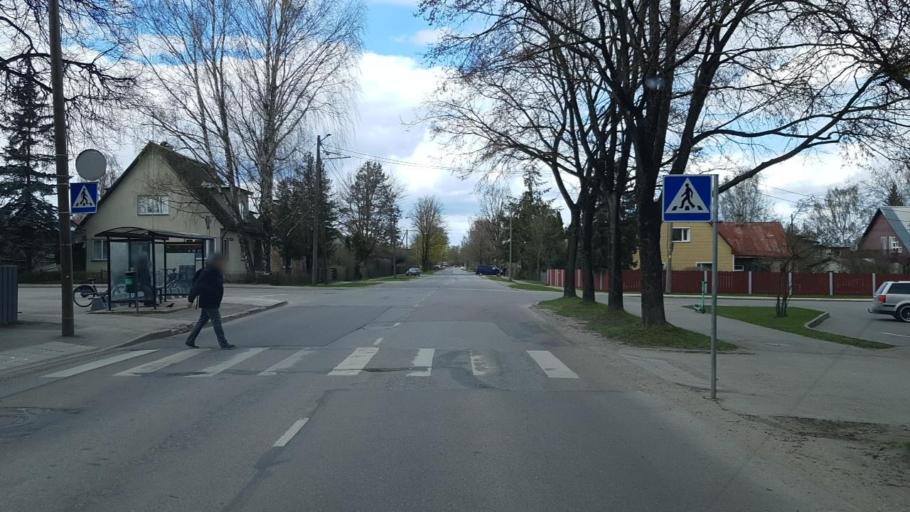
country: EE
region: Tartu
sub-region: Tartu linn
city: Tartu
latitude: 58.3499
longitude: 26.7234
